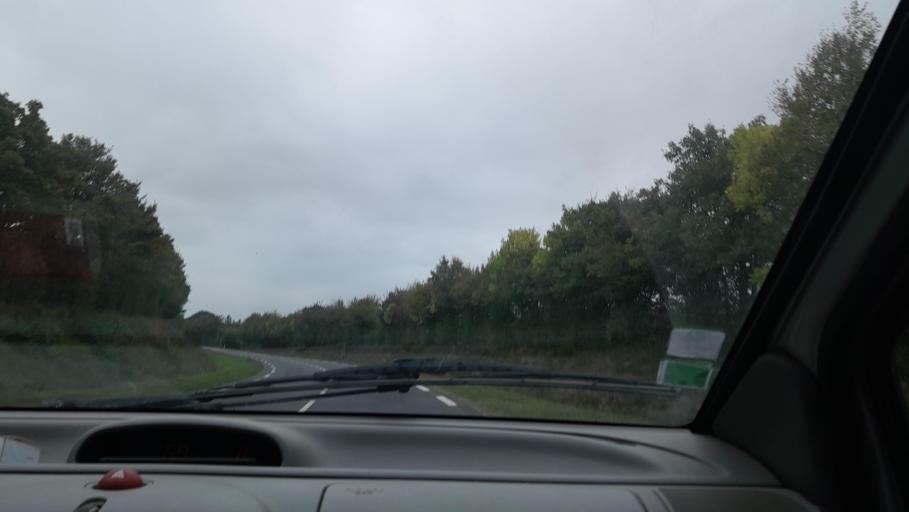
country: FR
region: Pays de la Loire
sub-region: Departement de la Loire-Atlantique
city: Saint-Mars-la-Jaille
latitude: 47.5284
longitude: -1.1791
